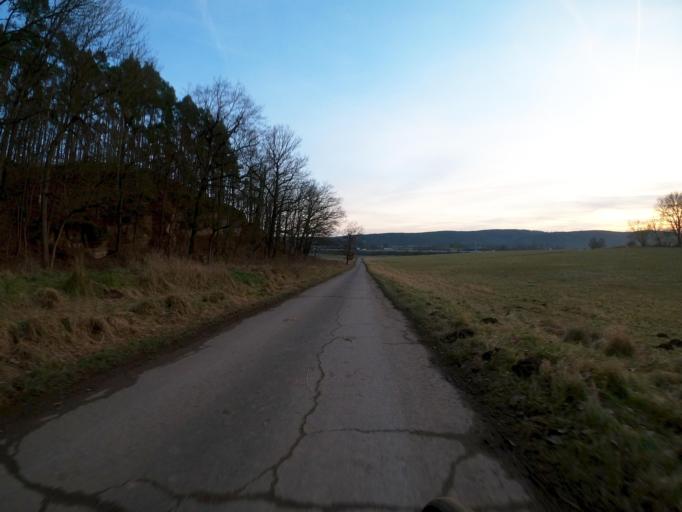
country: DE
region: Thuringia
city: Rausdorf
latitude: 50.8813
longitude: 11.6768
